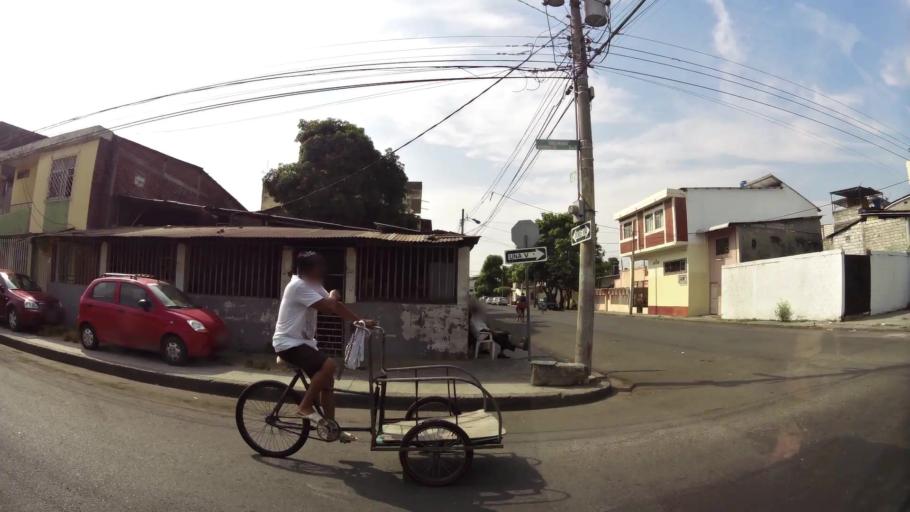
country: EC
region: Guayas
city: Guayaquil
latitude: -2.2166
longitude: -79.9055
